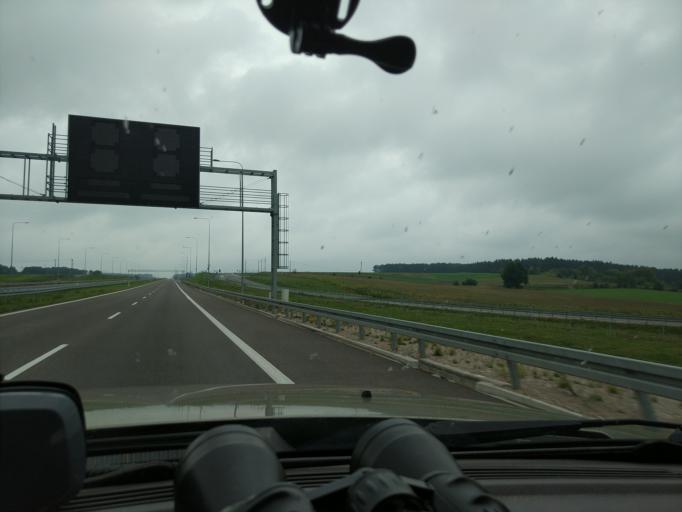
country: PL
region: Podlasie
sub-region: Powiat zambrowski
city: Rutki-Kossaki
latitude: 53.0545
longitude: 22.3894
